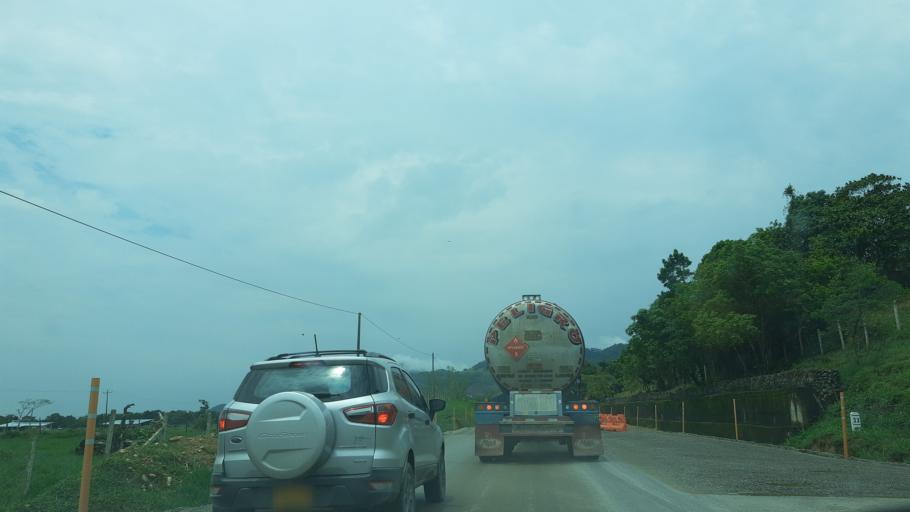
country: CO
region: Casanare
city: Sabanalarga
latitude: 4.7828
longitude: -72.9982
